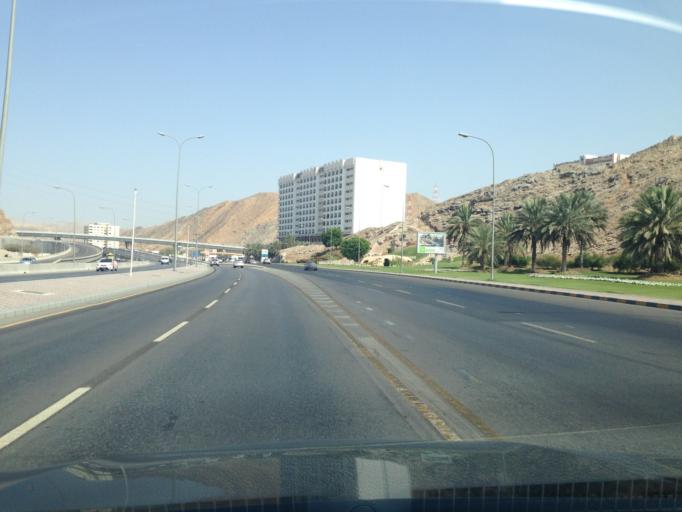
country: OM
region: Muhafazat Masqat
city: Muscat
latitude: 23.5944
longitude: 58.5219
